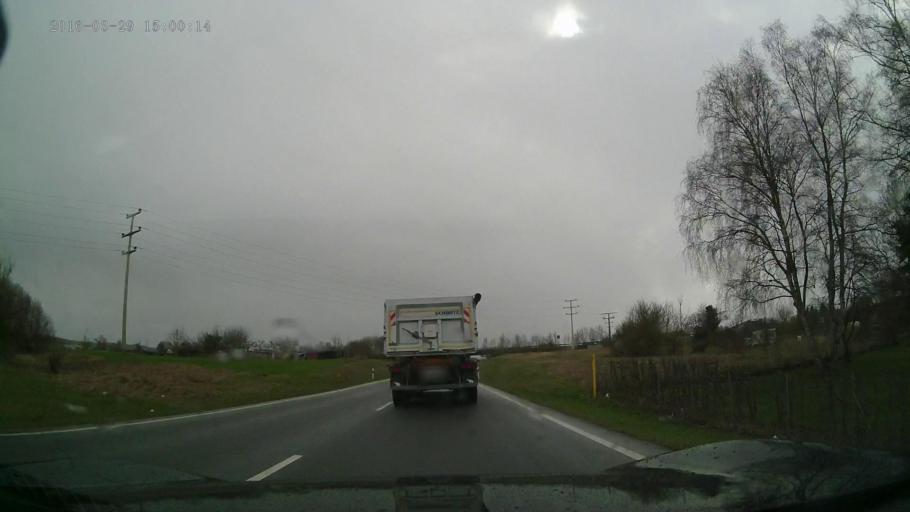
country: DE
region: Baden-Wuerttemberg
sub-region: Karlsruhe Region
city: Walldurn
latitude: 49.5809
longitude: 9.3775
